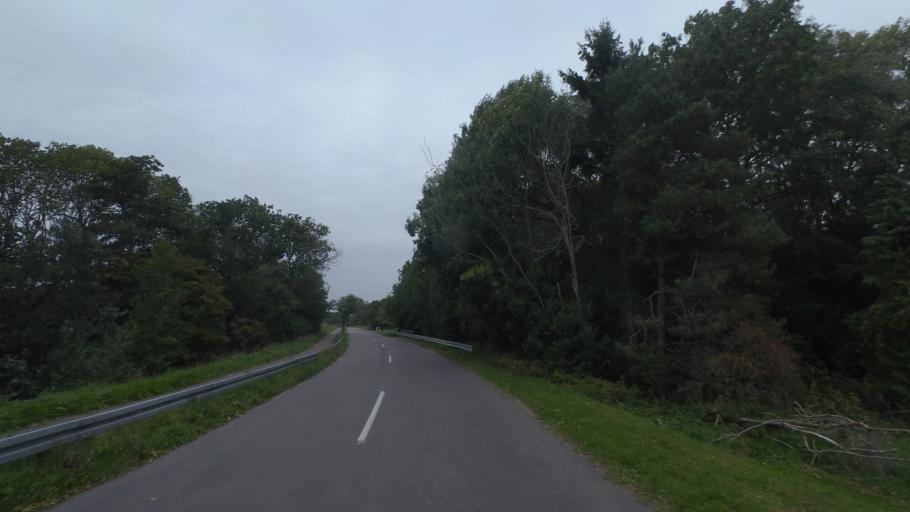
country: DK
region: Capital Region
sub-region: Bornholm Kommune
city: Akirkeby
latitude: 55.0081
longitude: 14.9964
